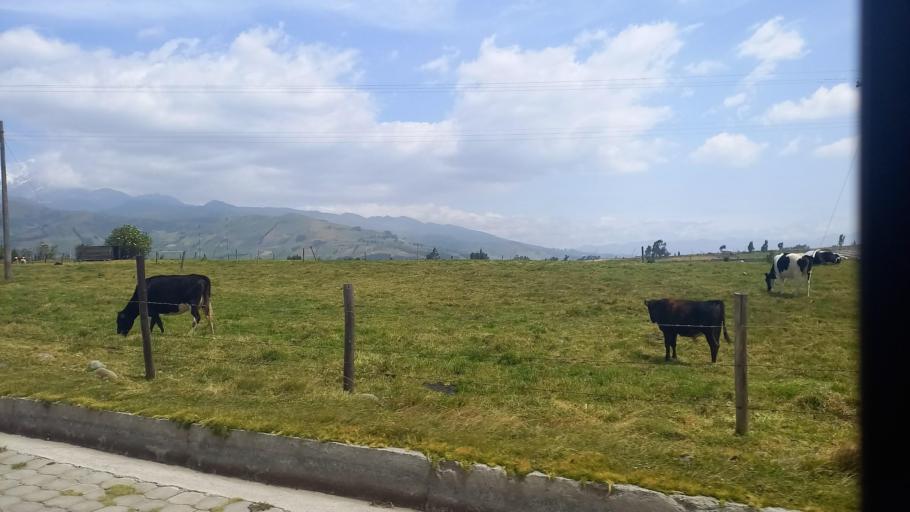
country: EC
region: Pichincha
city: Cayambe
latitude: 0.1578
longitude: -78.0738
